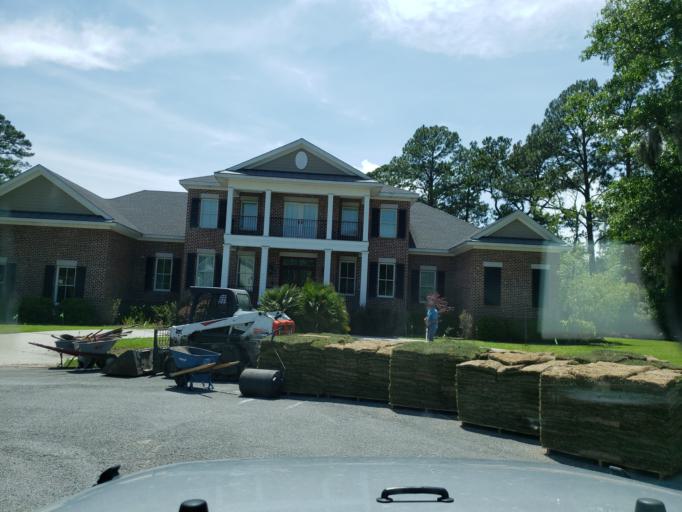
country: US
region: Georgia
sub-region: Chatham County
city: Whitemarsh Island
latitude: 32.0193
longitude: -81.0150
